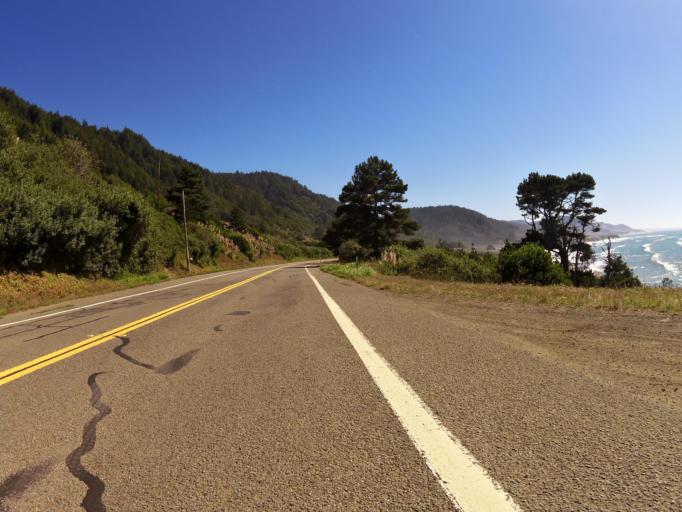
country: US
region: California
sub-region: Mendocino County
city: Fort Bragg
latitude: 39.6927
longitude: -123.7963
